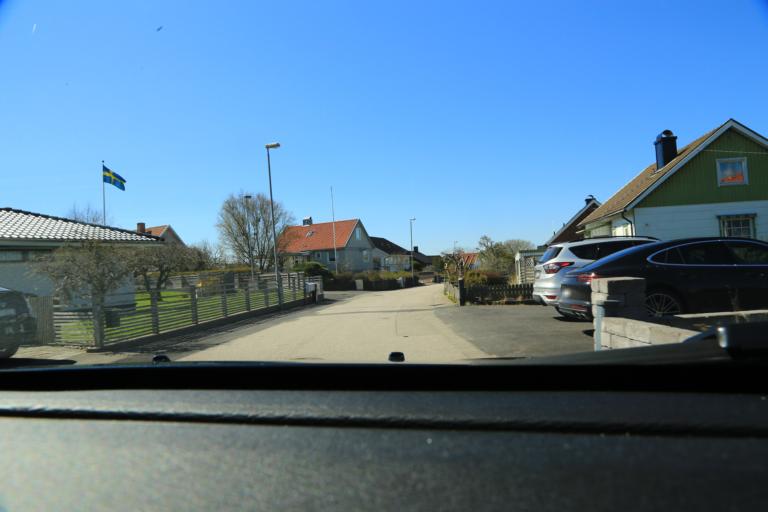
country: SE
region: Halland
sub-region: Varbergs Kommun
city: Traslovslage
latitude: 57.0605
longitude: 12.2804
